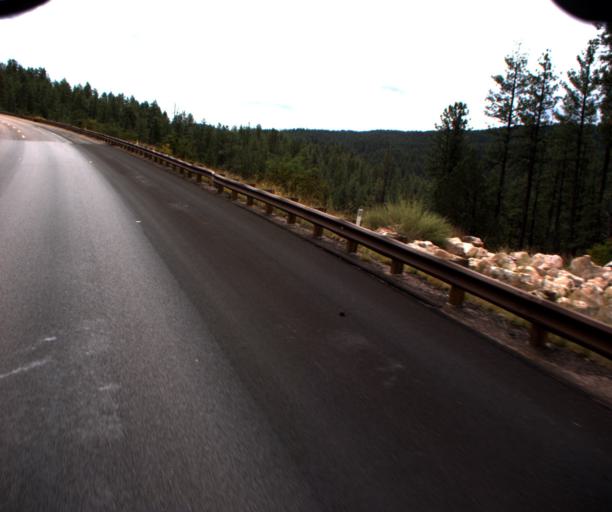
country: US
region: Arizona
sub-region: Gila County
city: Star Valley
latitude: 34.3096
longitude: -111.0237
